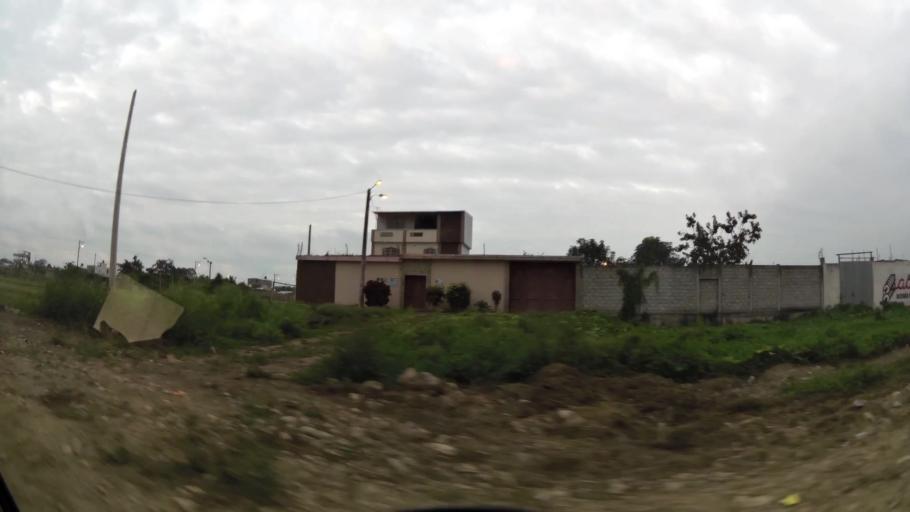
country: EC
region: El Oro
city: Machala
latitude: -3.2663
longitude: -79.9287
